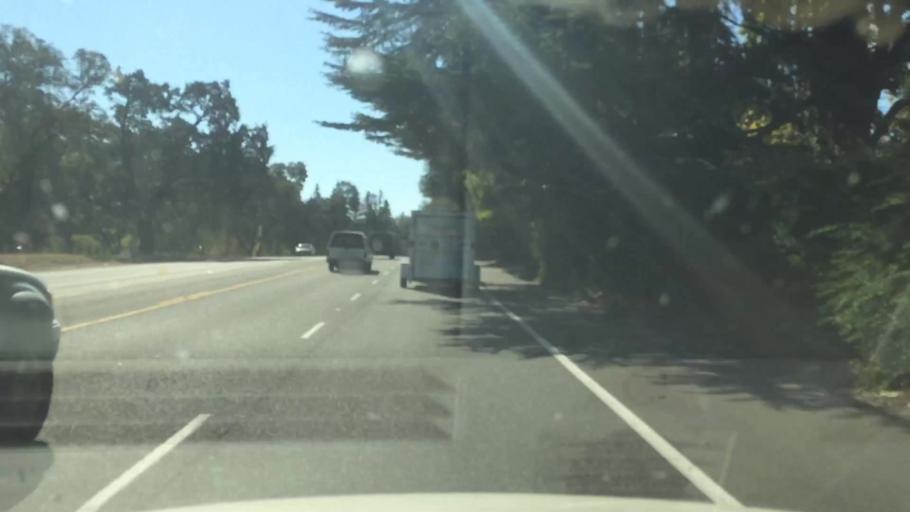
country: US
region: California
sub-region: Sacramento County
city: Orangevale
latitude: 38.6989
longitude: -121.2252
